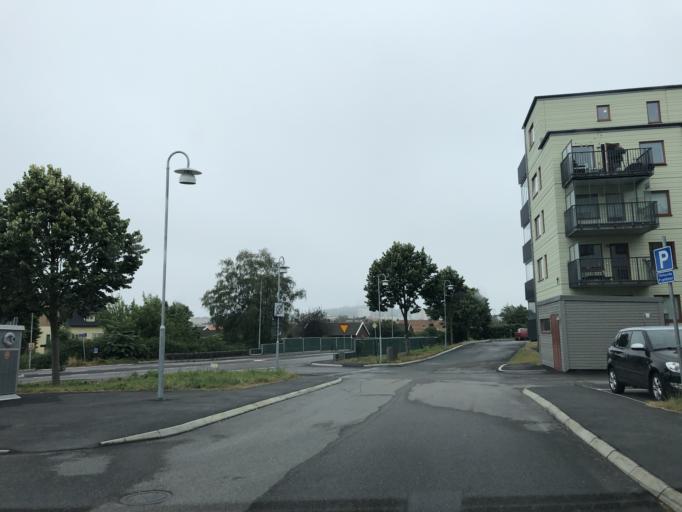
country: SE
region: Vaestra Goetaland
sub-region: Goteborg
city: Goeteborg
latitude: 57.7305
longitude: 11.9364
